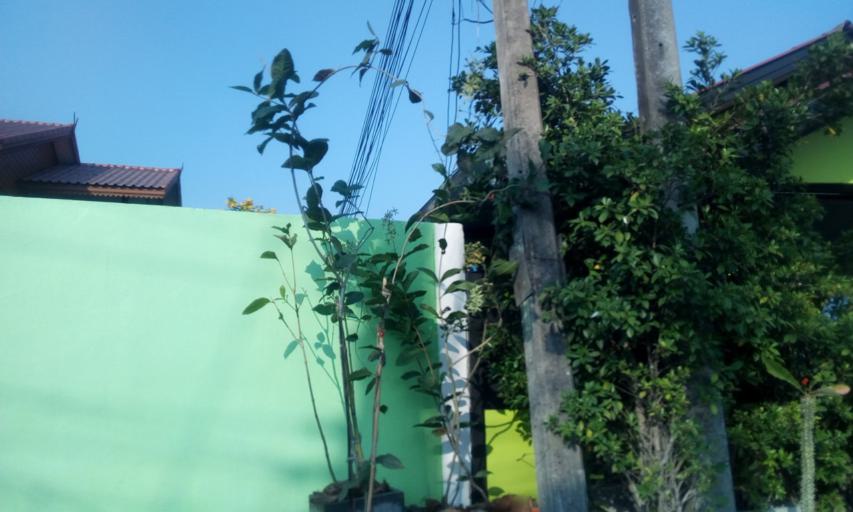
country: TH
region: Sing Buri
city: Sing Buri
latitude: 14.8358
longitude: 100.4017
